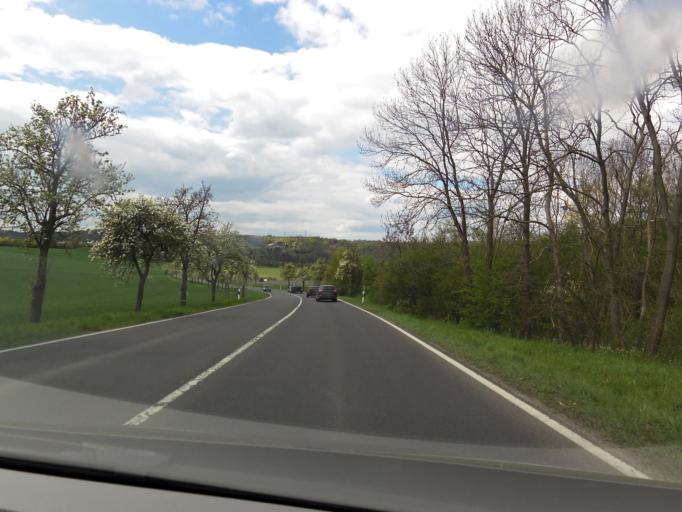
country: DE
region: Saxony-Anhalt
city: Bad Kosen
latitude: 51.1405
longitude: 11.7436
